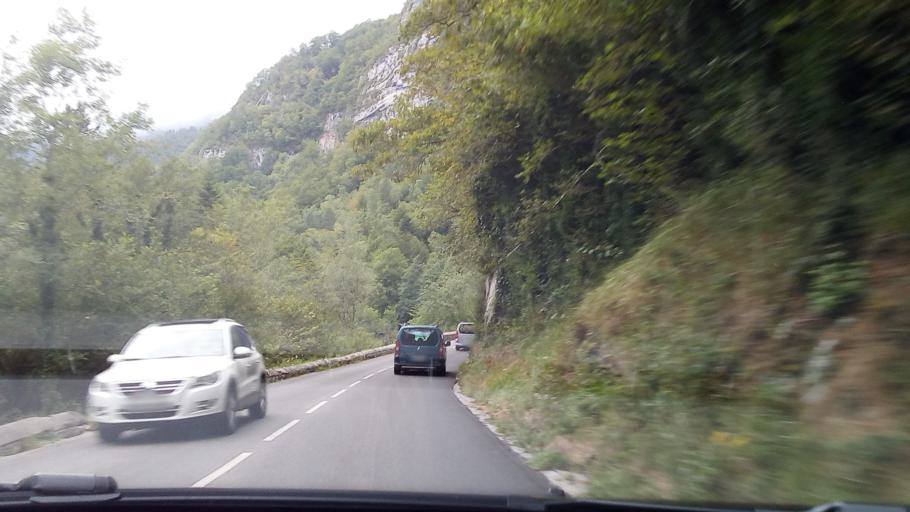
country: FR
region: Aquitaine
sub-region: Departement des Pyrenees-Atlantiques
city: Laruns
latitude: 42.9366
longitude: -0.4441
